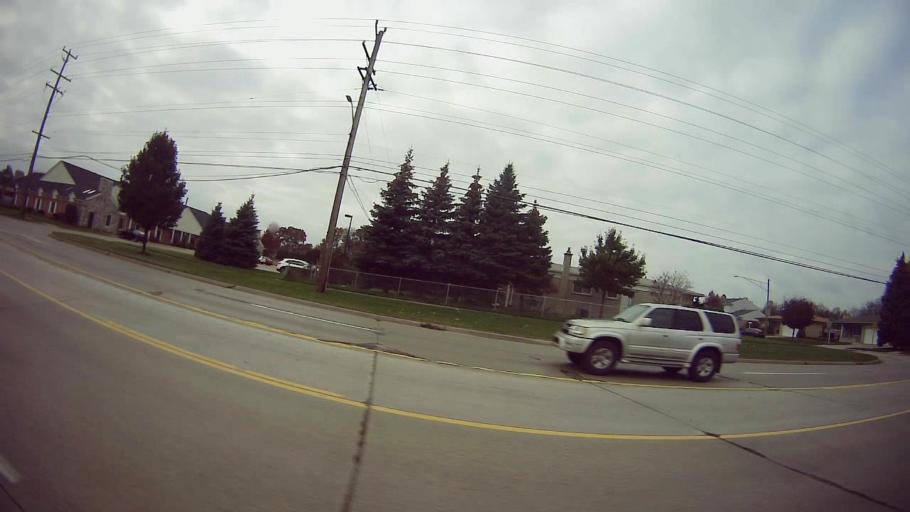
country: US
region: Michigan
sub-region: Oakland County
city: Madison Heights
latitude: 42.5063
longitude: -83.0677
